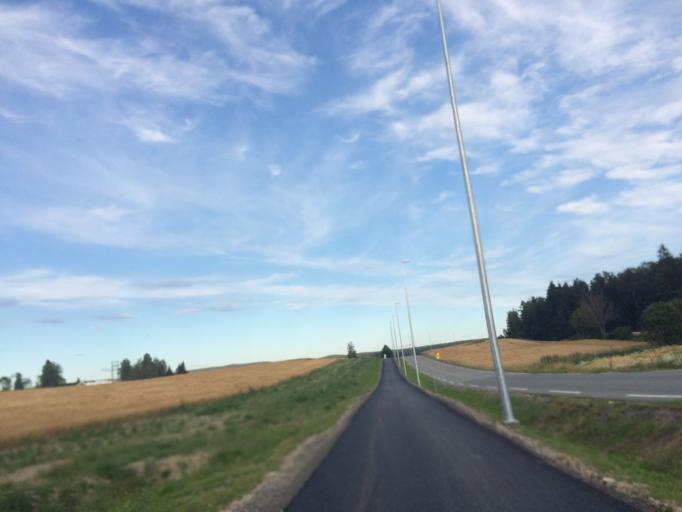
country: NO
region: Akershus
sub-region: Ski
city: Ski
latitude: 59.6968
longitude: 10.8530
